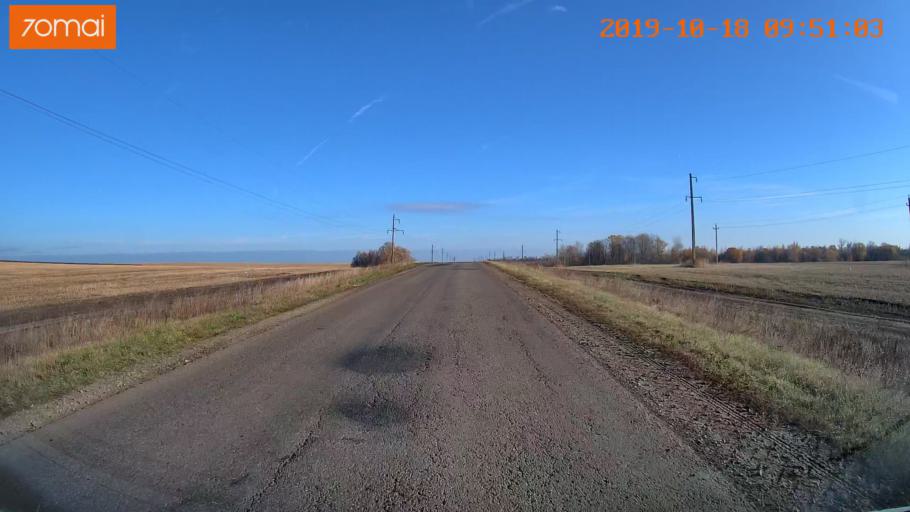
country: RU
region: Tula
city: Kazachka
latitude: 53.3357
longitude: 38.2864
